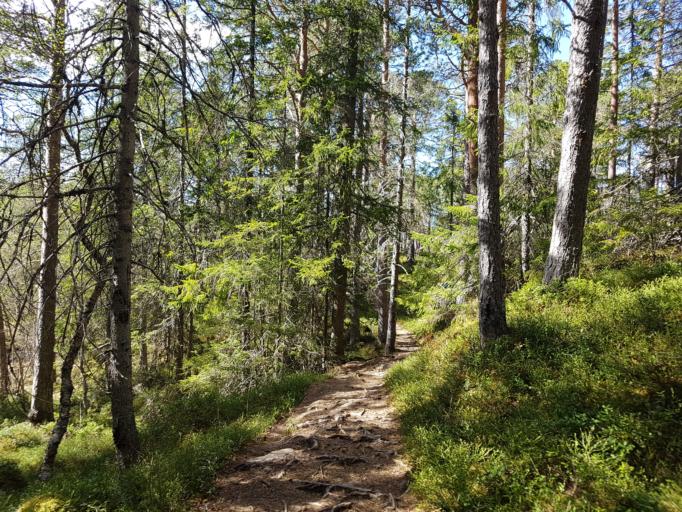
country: NO
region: Sor-Trondelag
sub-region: Trondheim
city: Trondheim
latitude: 63.4436
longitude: 10.3078
